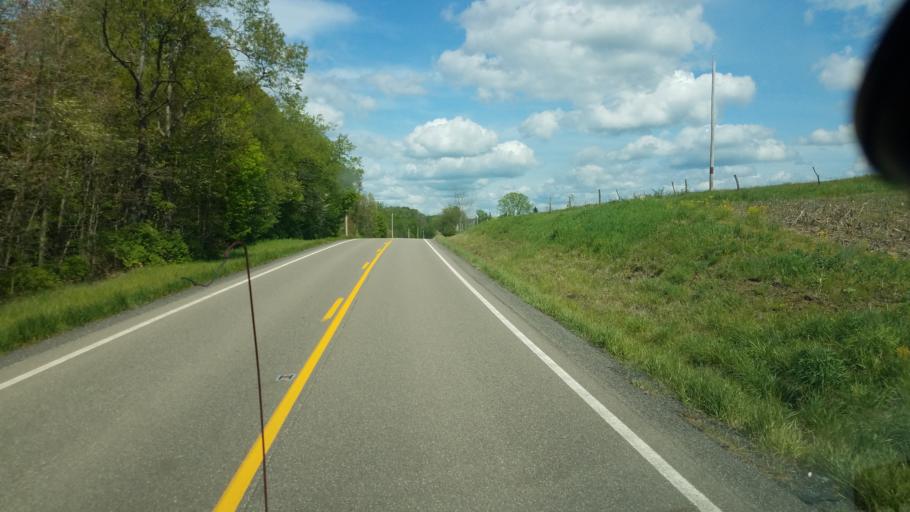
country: US
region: Ohio
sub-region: Knox County
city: Oak Hill
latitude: 40.2893
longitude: -82.2204
